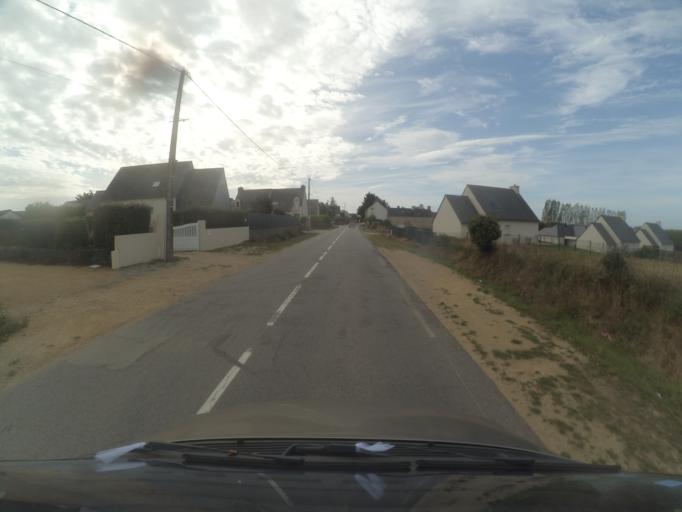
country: FR
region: Brittany
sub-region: Departement du Morbihan
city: Erdeven
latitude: 47.6244
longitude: -3.1608
